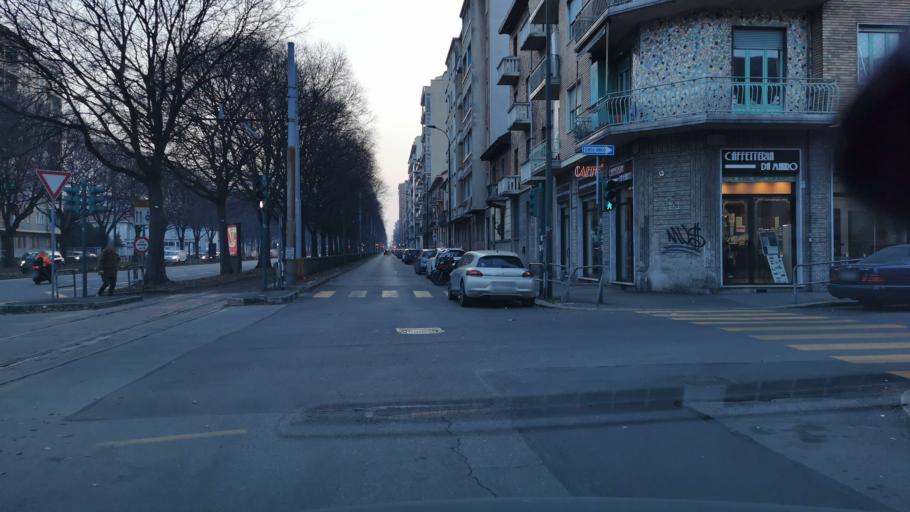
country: IT
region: Piedmont
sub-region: Provincia di Torino
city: Venaria Reale
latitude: 45.1005
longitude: 7.6601
